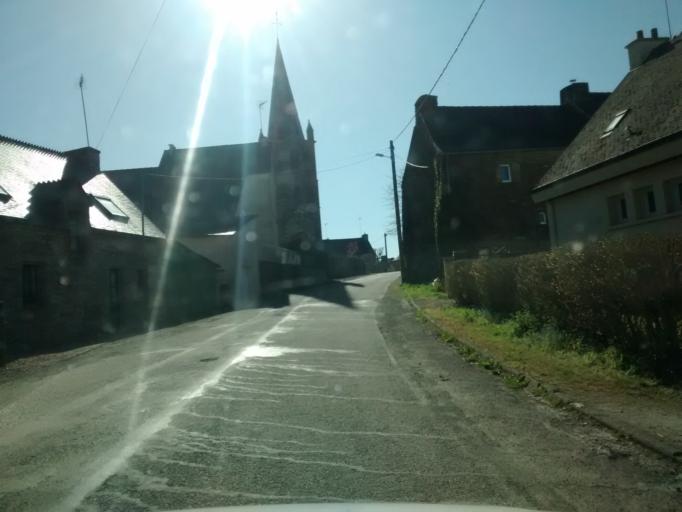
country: FR
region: Brittany
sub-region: Departement du Morbihan
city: Malestroit
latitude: 47.8564
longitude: -2.4107
